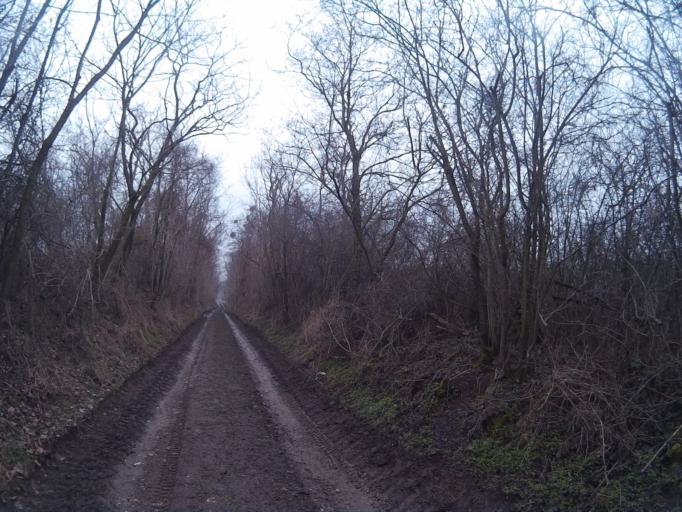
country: HU
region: Fejer
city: Szarliget
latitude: 47.5524
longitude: 18.5612
